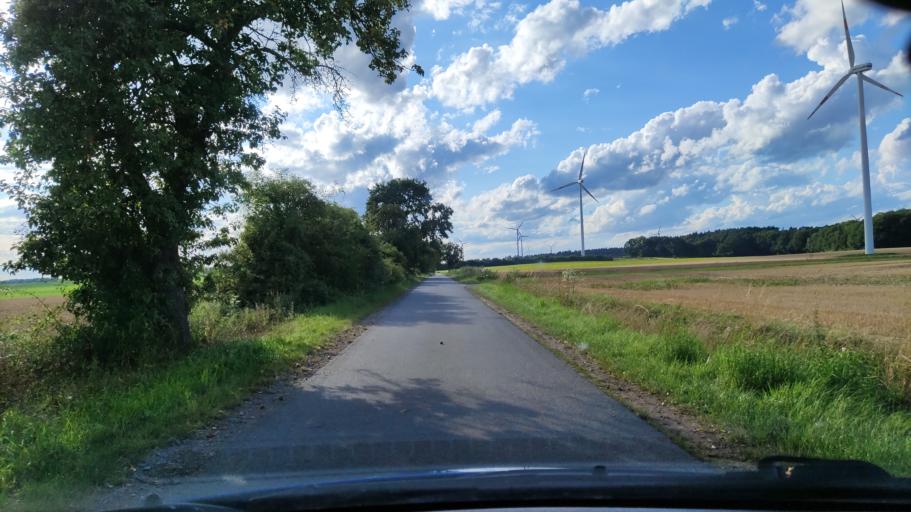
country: DE
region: Lower Saxony
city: Nahrendorf
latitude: 53.1759
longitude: 10.8054
